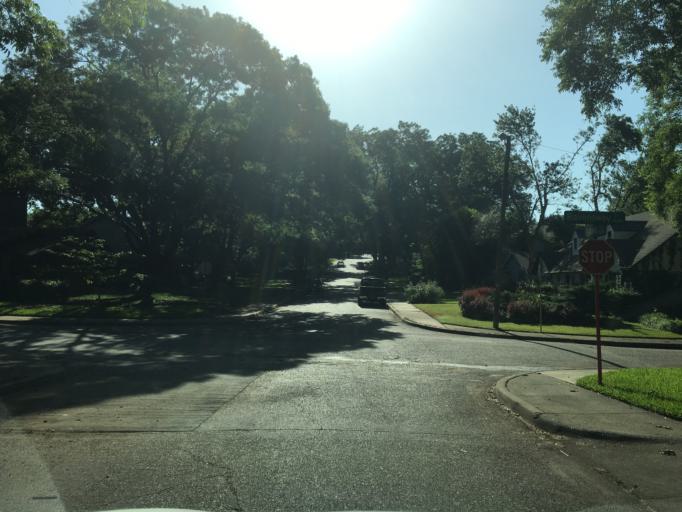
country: US
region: Texas
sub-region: Dallas County
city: Richardson
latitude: 32.8838
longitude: -96.7203
